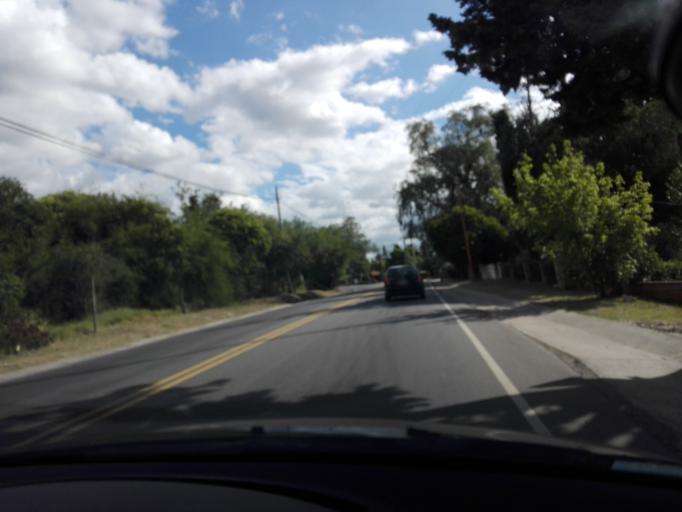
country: AR
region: Cordoba
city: Villa Las Rosas
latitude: -31.8927
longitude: -64.9880
